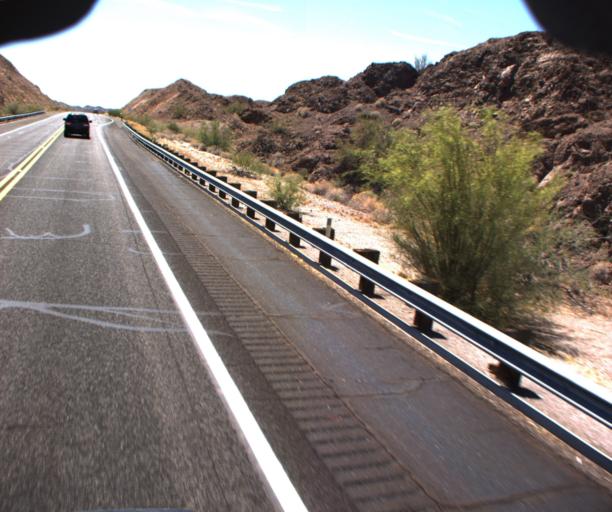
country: US
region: Arizona
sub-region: La Paz County
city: Cienega Springs
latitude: 34.2378
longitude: -114.1768
